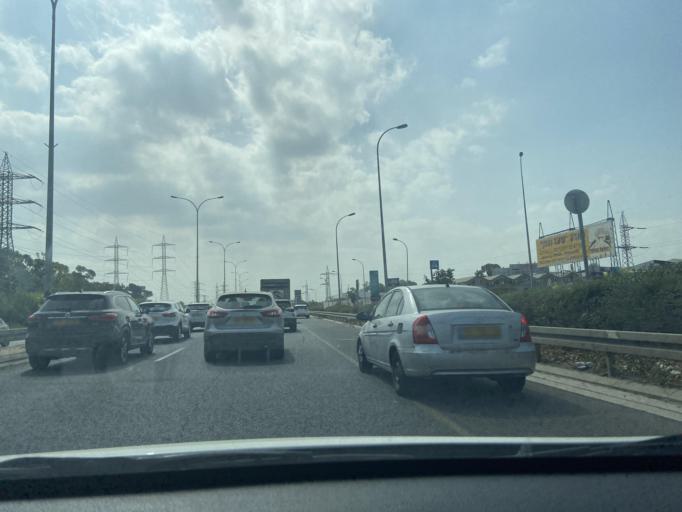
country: IL
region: Northern District
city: `Akko
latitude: 32.8941
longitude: 35.0938
